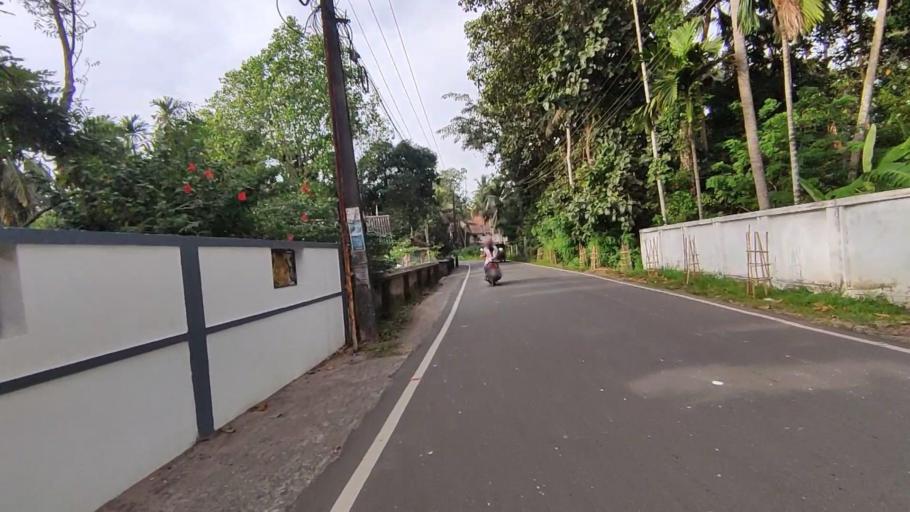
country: IN
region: Kerala
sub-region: Kottayam
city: Kottayam
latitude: 9.6013
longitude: 76.5035
